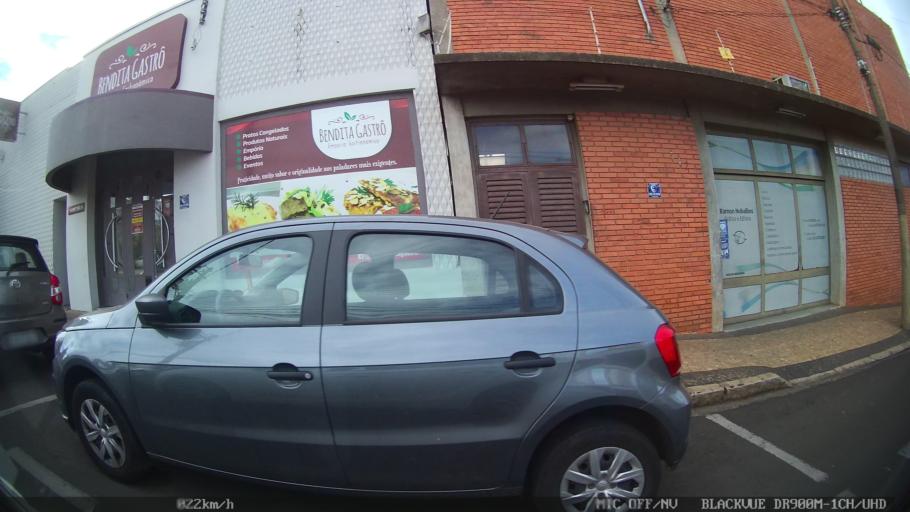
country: BR
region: Sao Paulo
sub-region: Catanduva
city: Catanduva
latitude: -21.1285
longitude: -48.9681
